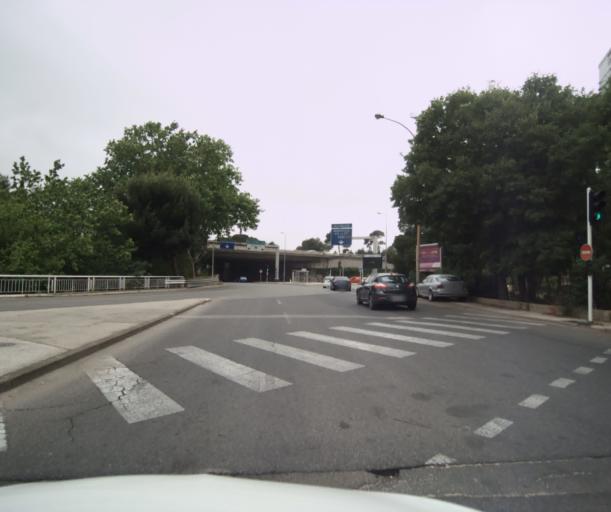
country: FR
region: Provence-Alpes-Cote d'Azur
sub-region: Departement du Var
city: La Seyne-sur-Mer
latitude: 43.1266
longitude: 5.8980
